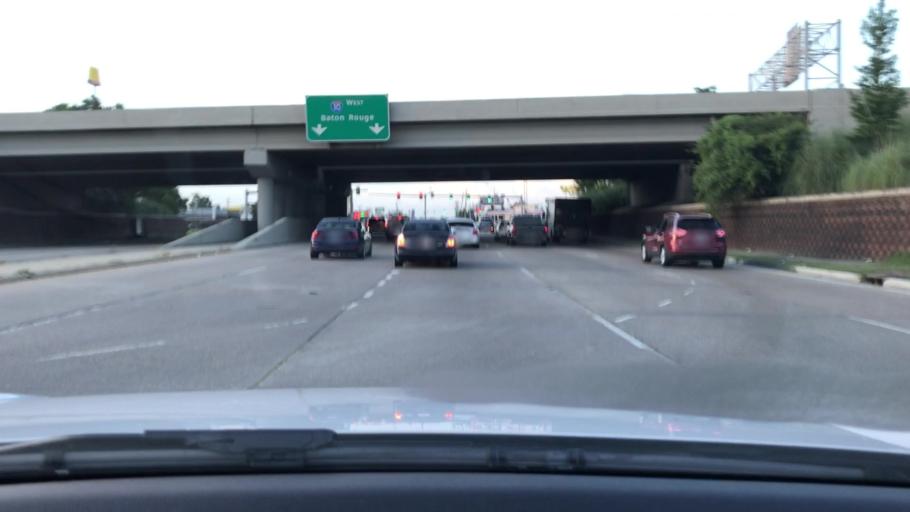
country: US
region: Louisiana
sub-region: East Baton Rouge Parish
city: Village Saint George
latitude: 30.3817
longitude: -91.0663
